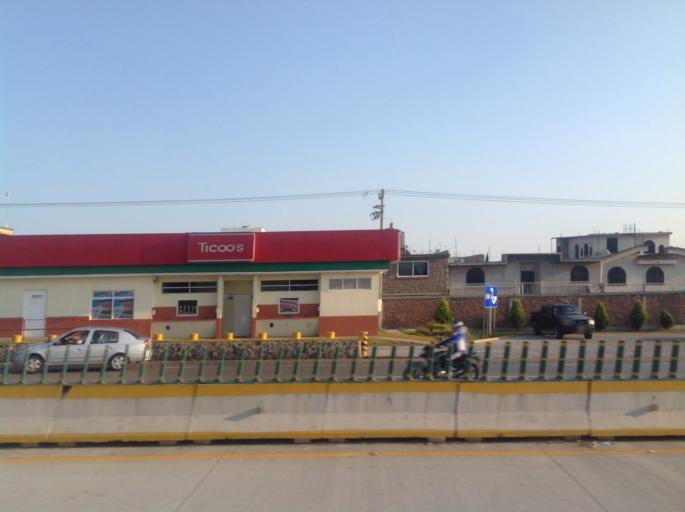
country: MX
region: Mexico
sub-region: Ixtapaluca
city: San Buenaventura
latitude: 19.2971
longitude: -98.8681
